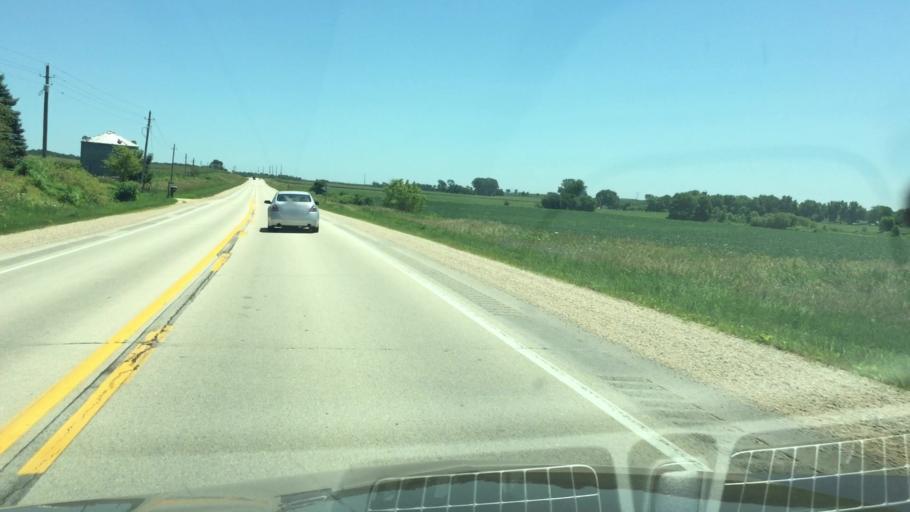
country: US
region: Iowa
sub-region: Jackson County
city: Maquoketa
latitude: 42.0695
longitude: -90.7921
